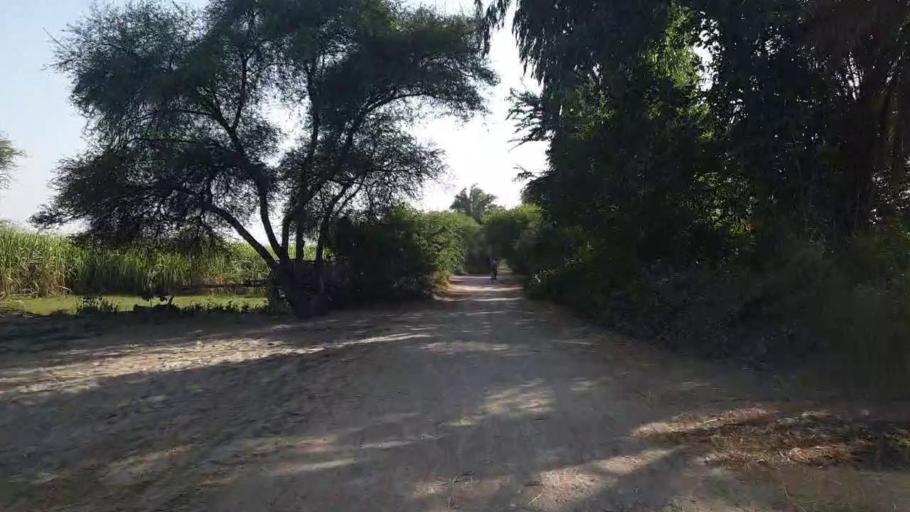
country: PK
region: Sindh
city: Matli
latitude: 25.0143
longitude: 68.7404
